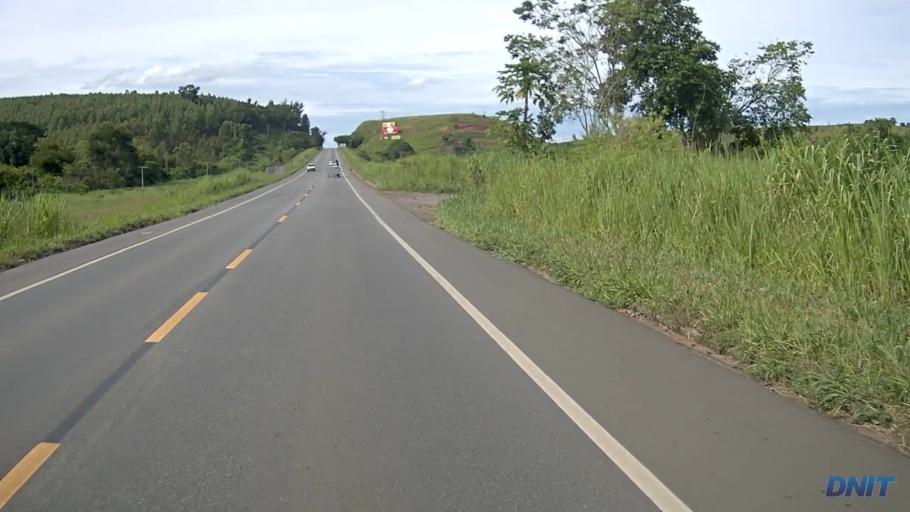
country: BR
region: Minas Gerais
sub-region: Belo Oriente
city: Belo Oriente
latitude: -19.2565
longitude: -42.3416
